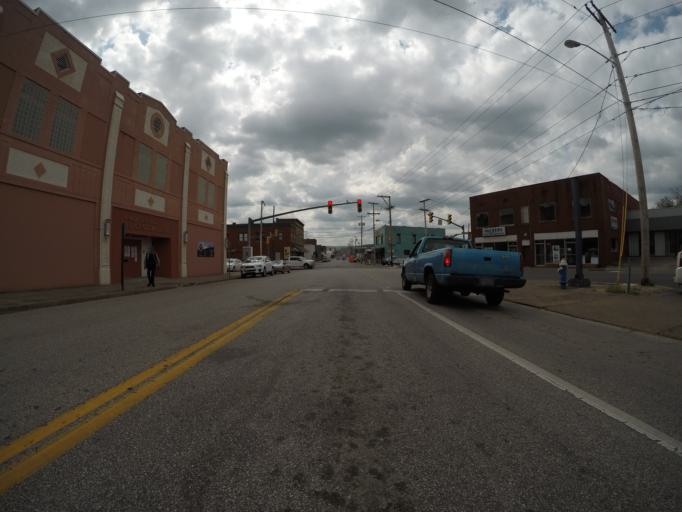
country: US
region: West Virginia
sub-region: Kanawha County
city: Charleston
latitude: 38.3623
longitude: -81.6491
